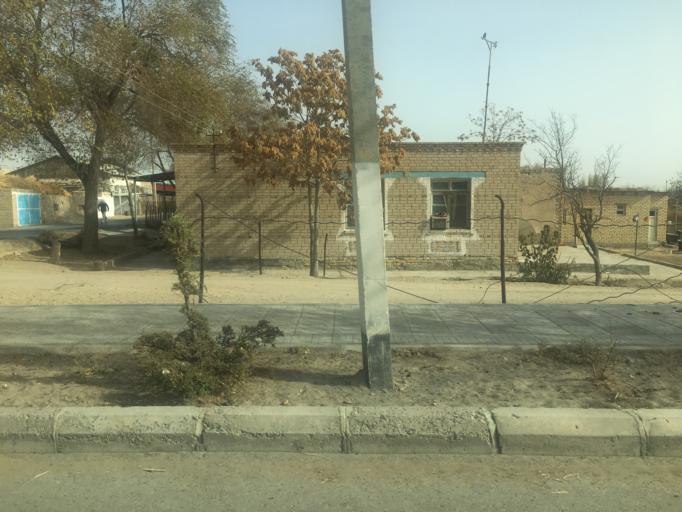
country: TM
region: Lebap
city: Gazojak
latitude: 41.1833
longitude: 61.4029
